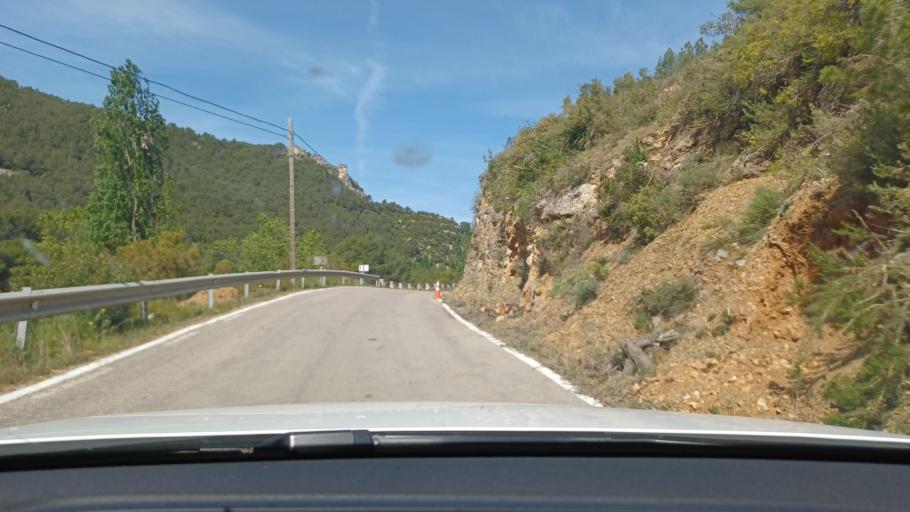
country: ES
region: Valencia
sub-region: Provincia de Castello
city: Rosell
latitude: 40.6704
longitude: 0.2448
